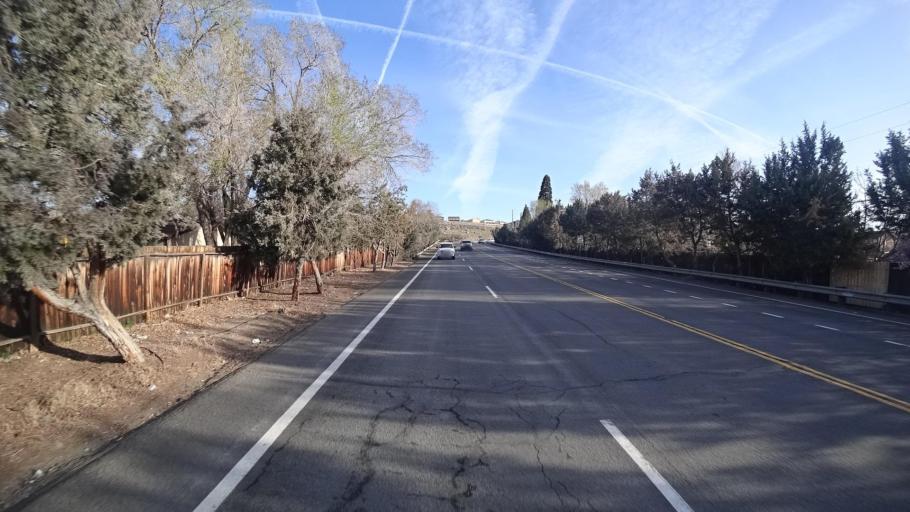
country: US
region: Nevada
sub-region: Washoe County
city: Sparks
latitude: 39.5556
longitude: -119.7793
